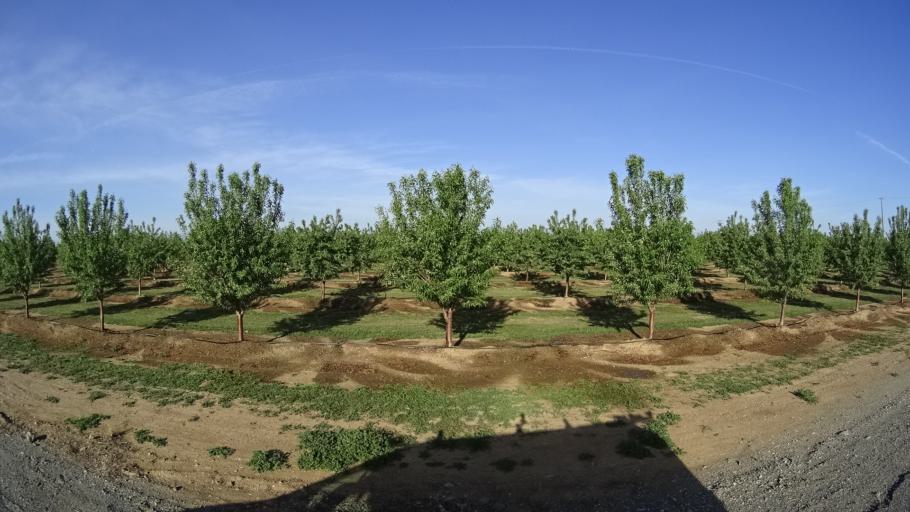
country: US
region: California
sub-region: Glenn County
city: Orland
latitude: 39.7252
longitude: -122.2347
